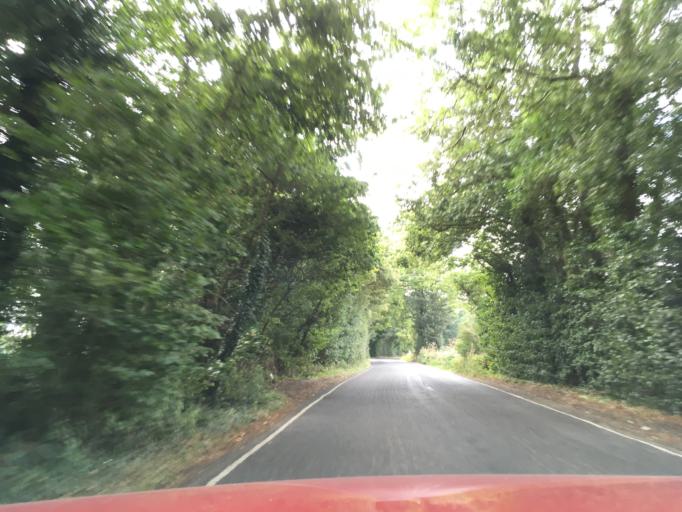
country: GB
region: England
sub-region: Kent
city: Headcorn
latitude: 51.2218
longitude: 0.5840
